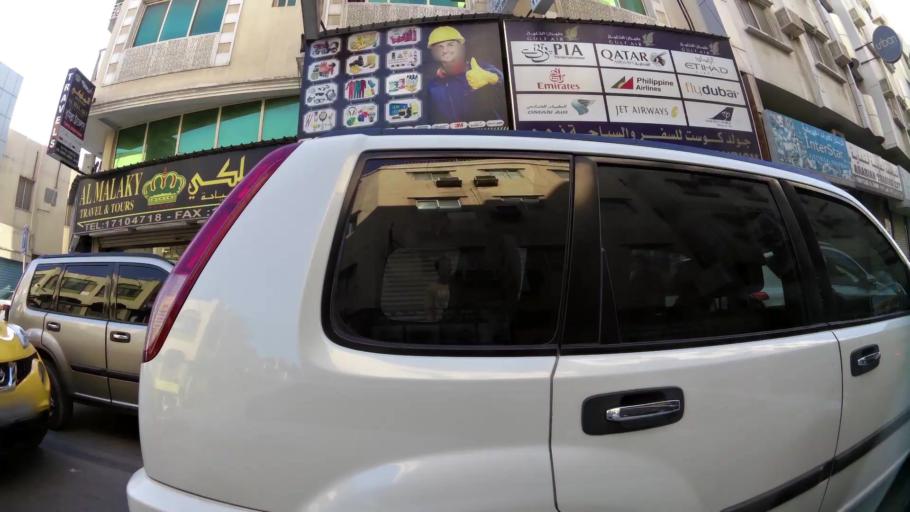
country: BH
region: Manama
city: Manama
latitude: 26.2295
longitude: 50.5713
